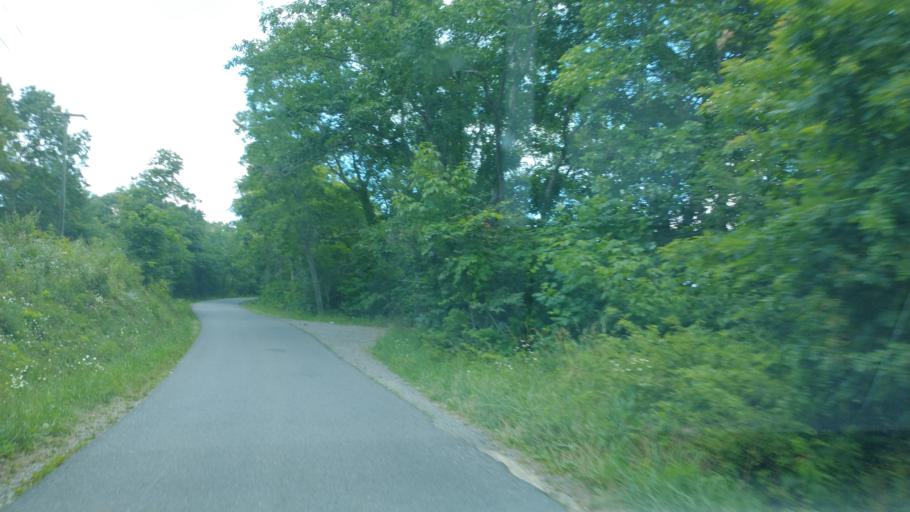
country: US
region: West Virginia
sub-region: Mercer County
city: Athens
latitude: 37.4599
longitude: -81.0594
